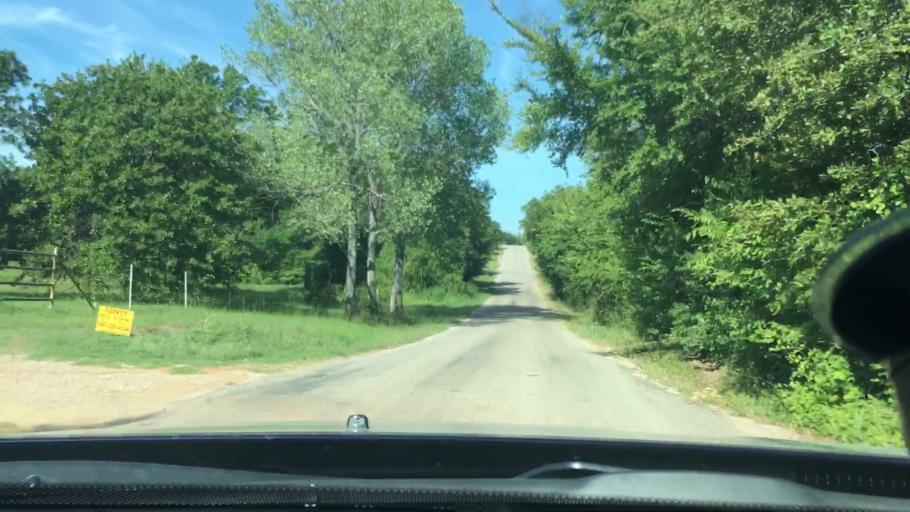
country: US
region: Oklahoma
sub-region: Carter County
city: Lone Grove
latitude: 34.2674
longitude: -97.2747
